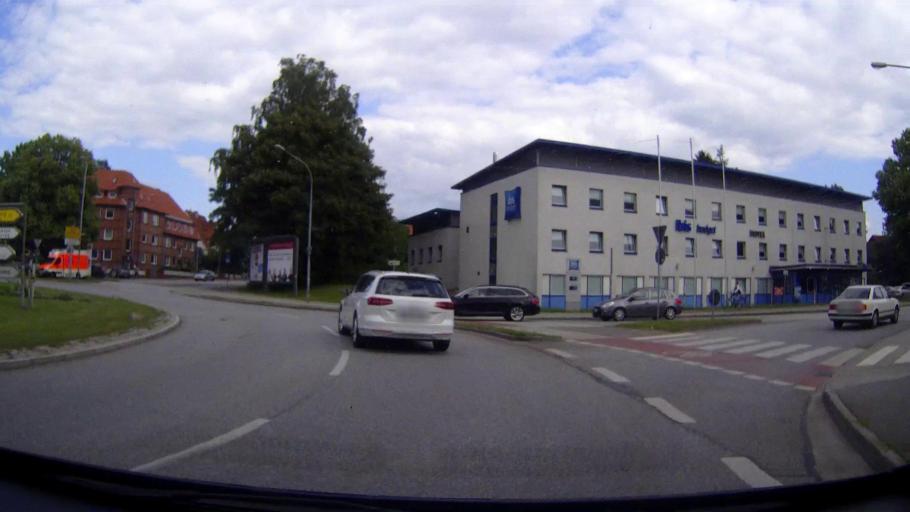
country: DE
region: Schleswig-Holstein
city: Luebeck
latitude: 53.8507
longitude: 10.6822
